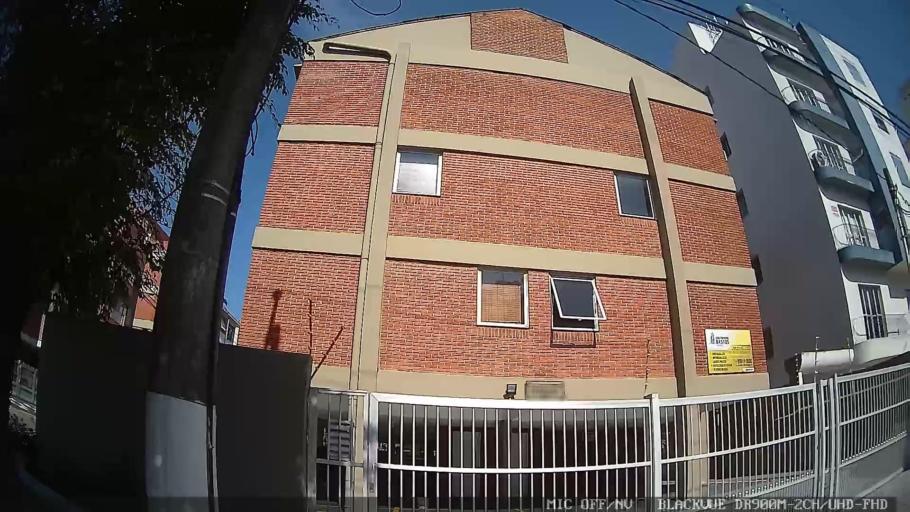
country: BR
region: Sao Paulo
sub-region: Guaruja
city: Guaruja
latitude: -24.0090
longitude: -46.2732
